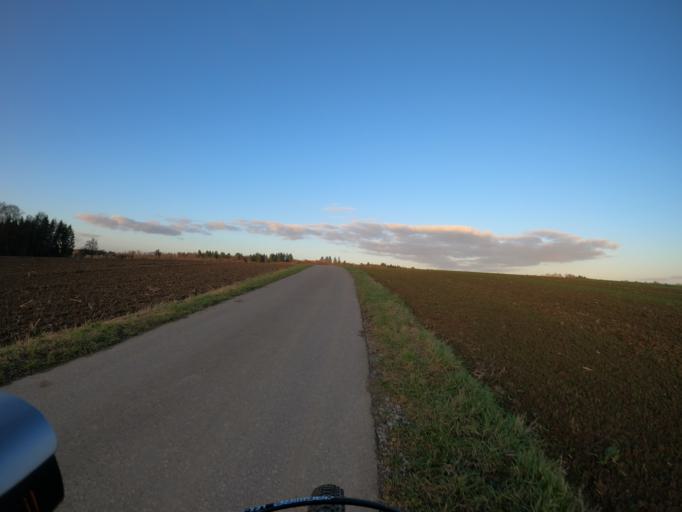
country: DE
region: Baden-Wuerttemberg
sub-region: Regierungsbezirk Stuttgart
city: Schlierbach
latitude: 48.6730
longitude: 9.4956
